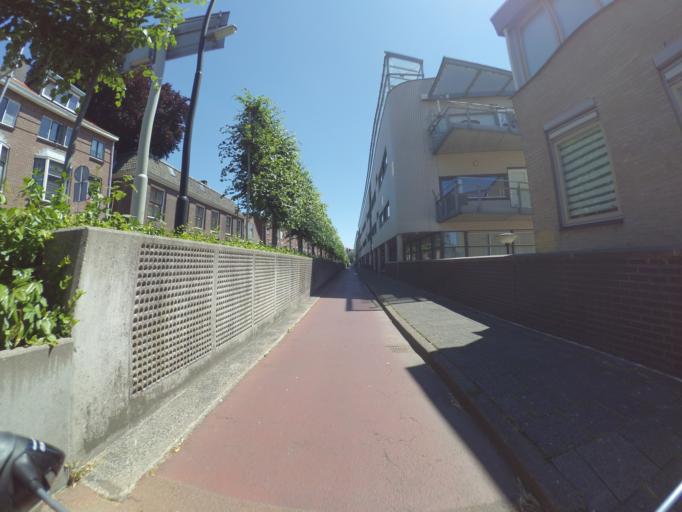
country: NL
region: South Holland
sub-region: Gemeente Dordrecht
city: Dordrecht
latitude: 51.8161
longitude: 4.6759
